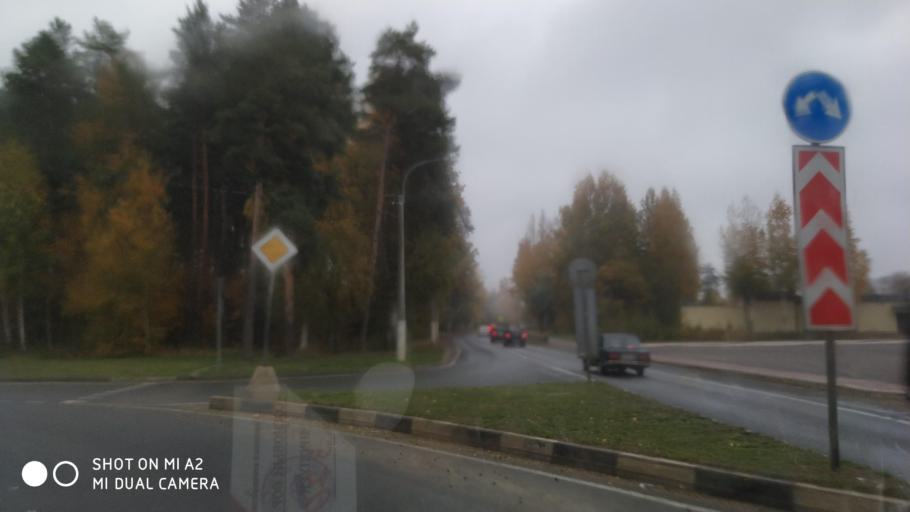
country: RU
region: Leningrad
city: Sosnovyy Bor
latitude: 59.8945
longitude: 29.1130
